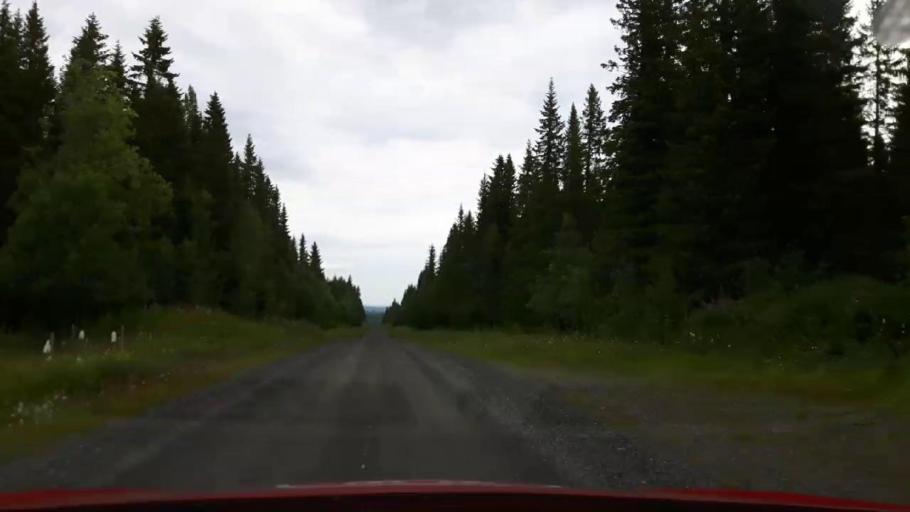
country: SE
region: Jaemtland
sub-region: OEstersunds Kommun
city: Lit
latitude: 63.3857
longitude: 15.2017
